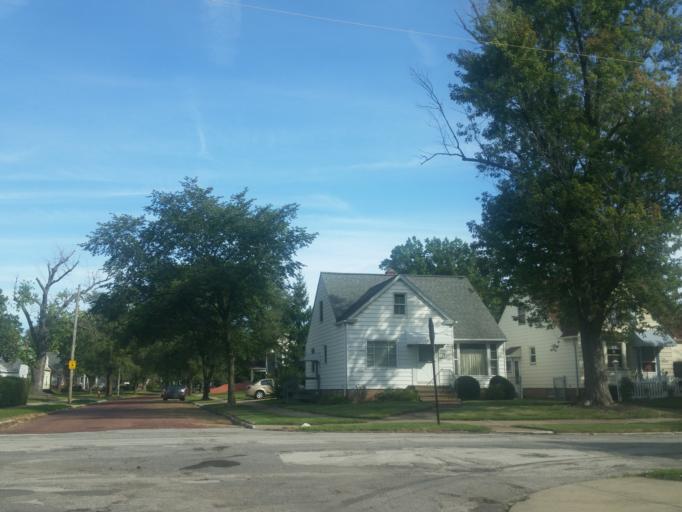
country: US
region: Ohio
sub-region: Cuyahoga County
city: Lakewood
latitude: 41.4684
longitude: -81.8007
